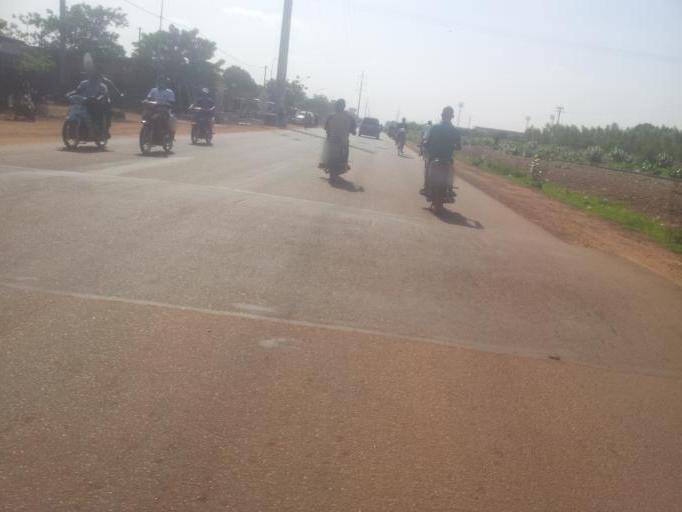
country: BF
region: Centre
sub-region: Kadiogo Province
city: Ouagadougou
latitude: 12.3698
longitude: -1.5634
